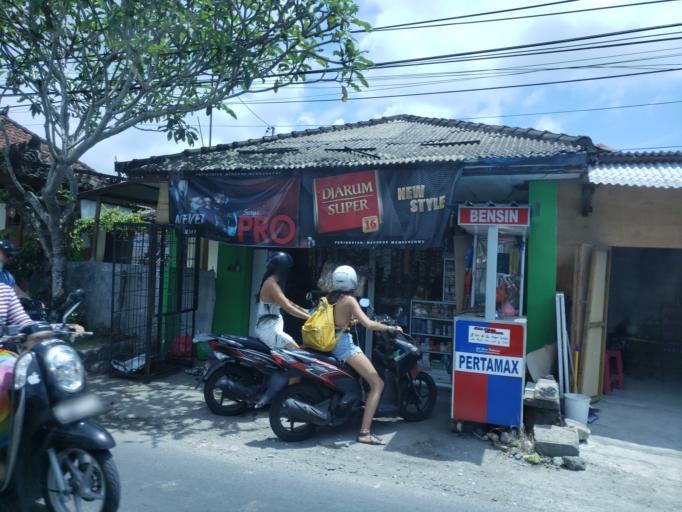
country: ID
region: Bali
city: Jimbaran
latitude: -8.8187
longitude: 115.1538
